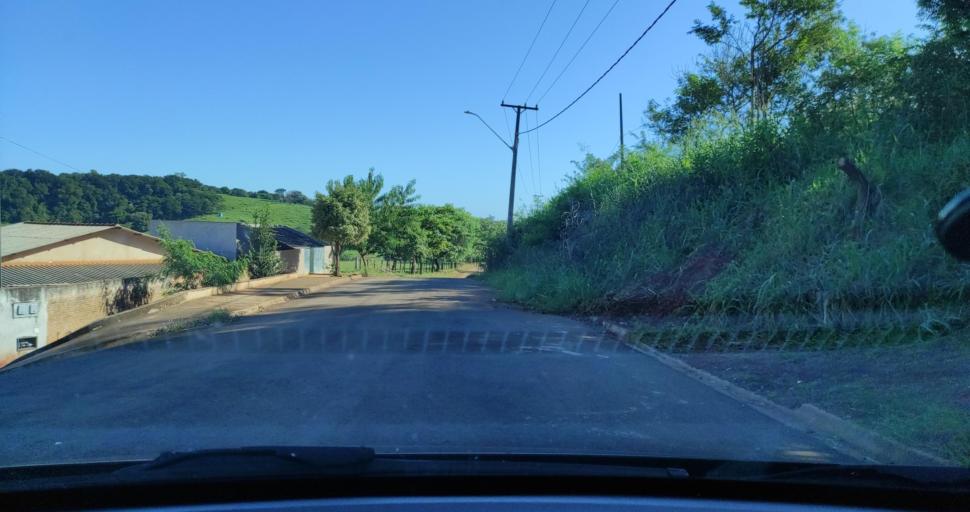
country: BR
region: Parana
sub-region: Ibipora
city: Ibipora
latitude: -23.2592
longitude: -51.0632
